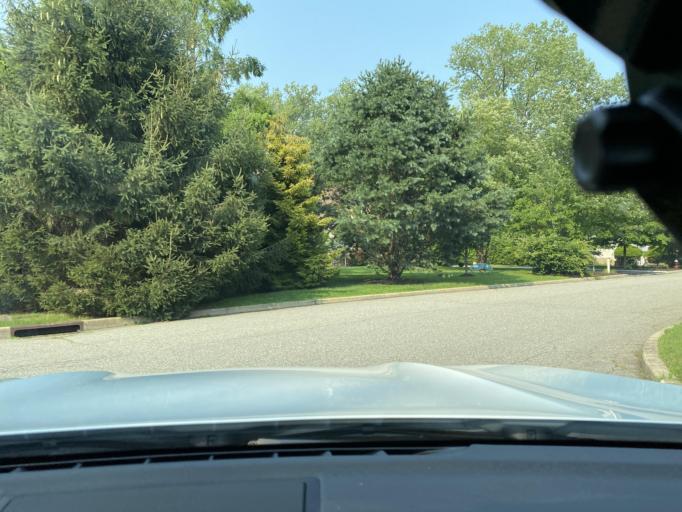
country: US
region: New York
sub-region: Rockland County
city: Airmont
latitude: 41.0829
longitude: -74.1193
